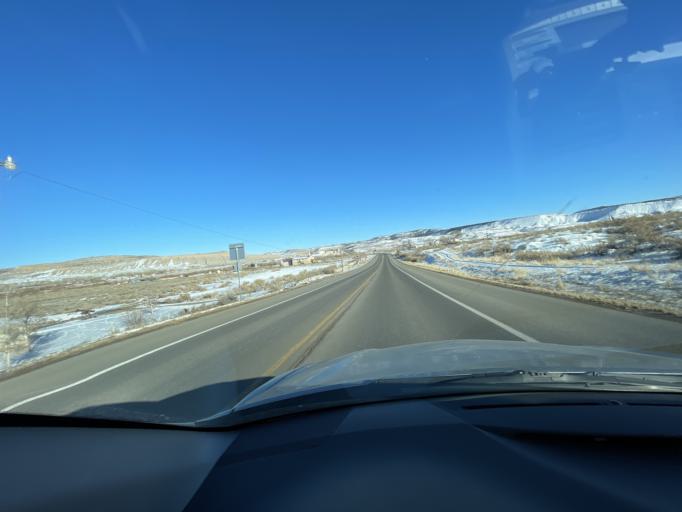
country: US
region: Colorado
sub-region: Rio Blanco County
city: Rangely
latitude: 40.0876
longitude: -108.7831
